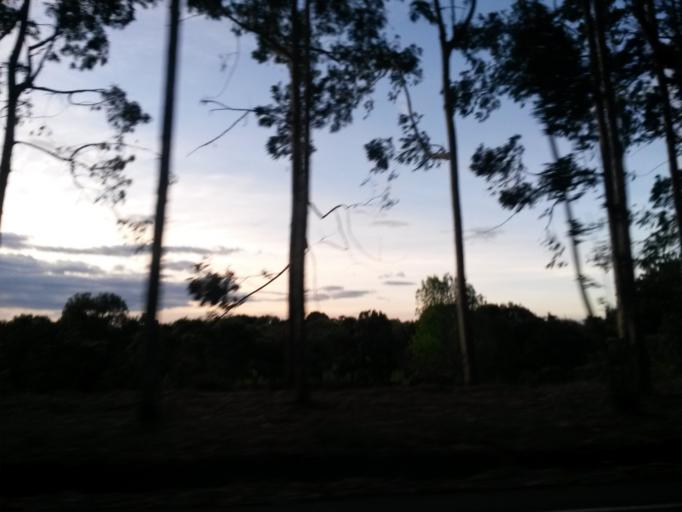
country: CO
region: Cauca
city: Popayan
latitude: 2.4792
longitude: -76.5898
